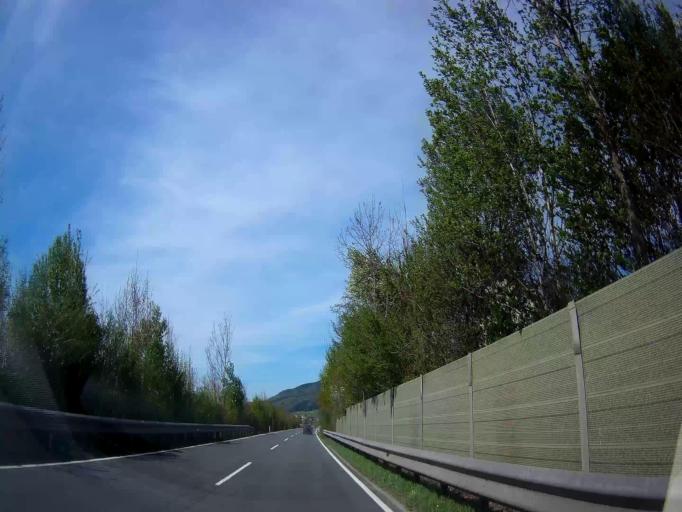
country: AT
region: Salzburg
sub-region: Politischer Bezirk Salzburg-Umgebung
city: Anthering
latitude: 47.8809
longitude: 13.0033
